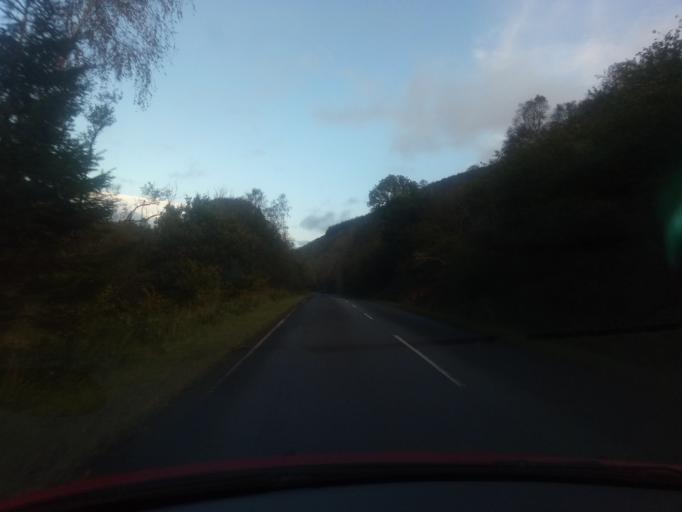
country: GB
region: Scotland
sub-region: The Scottish Borders
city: Hawick
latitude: 55.3547
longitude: -2.6481
